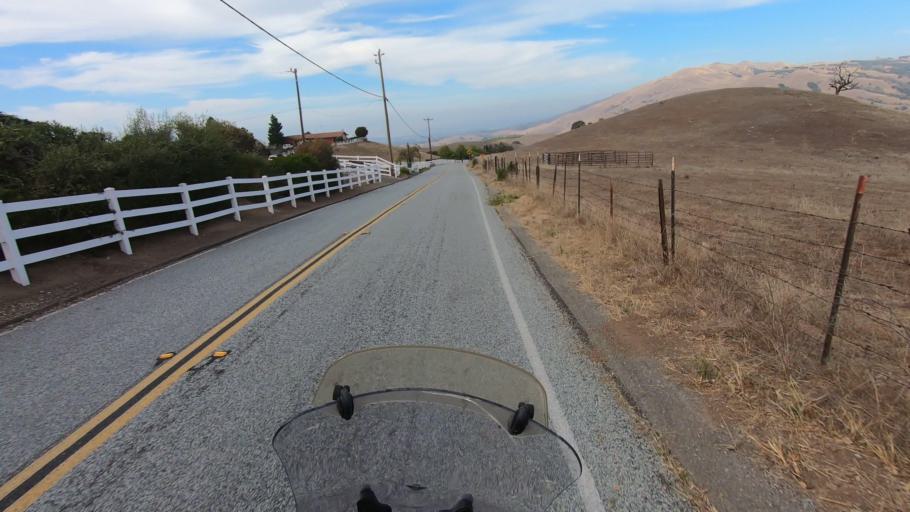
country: US
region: California
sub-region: Santa Clara County
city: East Foothills
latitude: 37.4340
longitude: -121.8172
